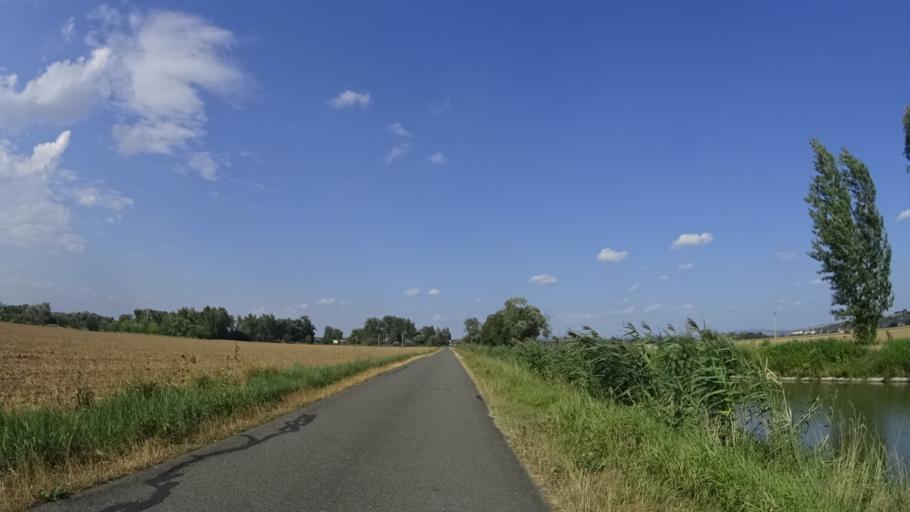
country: CZ
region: Zlin
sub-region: Okres Uherske Hradiste
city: Uherske Hradiste
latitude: 49.0807
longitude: 17.4621
